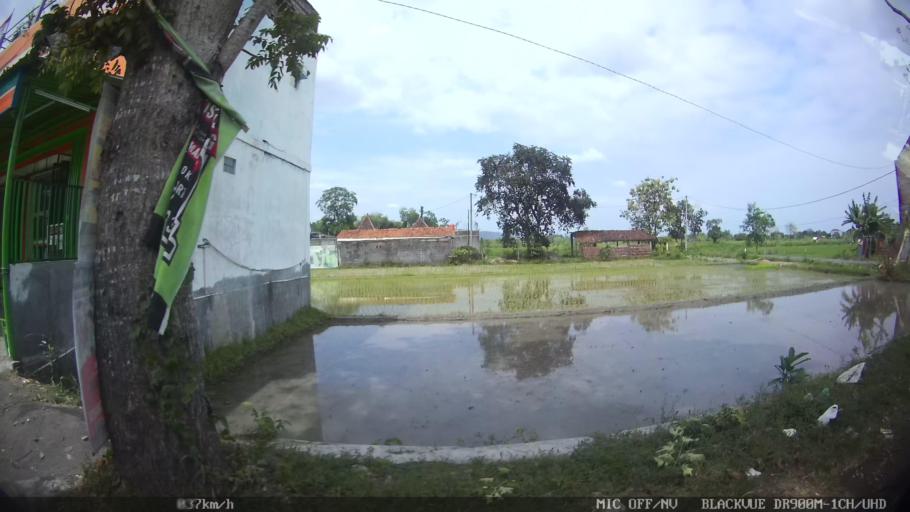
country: ID
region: Daerah Istimewa Yogyakarta
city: Depok
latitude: -7.8051
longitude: 110.4495
